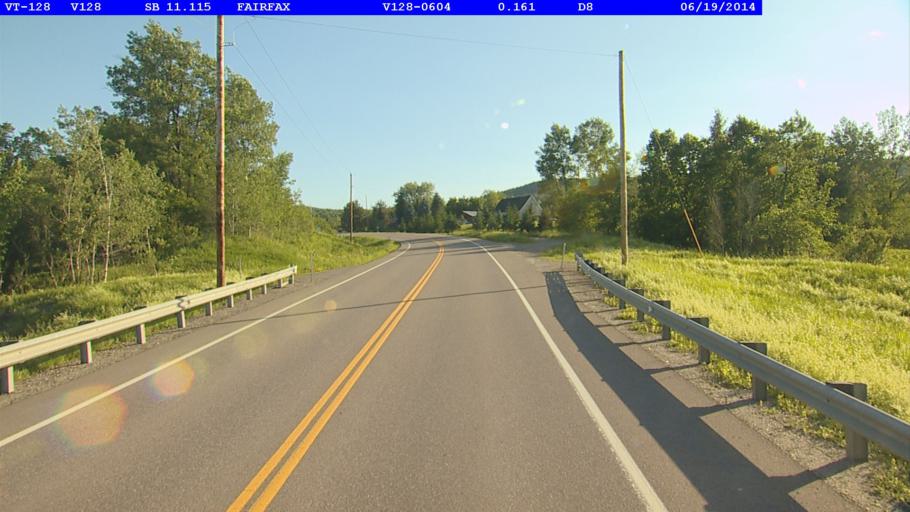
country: US
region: Vermont
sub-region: Chittenden County
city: Milton
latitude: 44.6493
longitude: -73.0128
